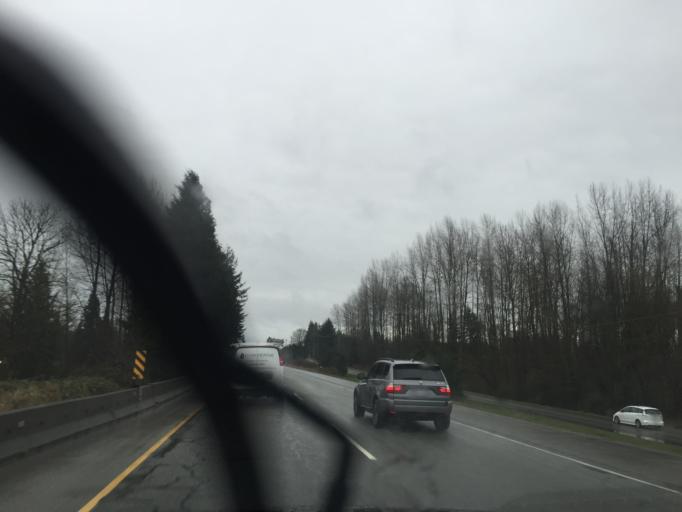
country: CA
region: British Columbia
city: Aldergrove
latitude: 49.0948
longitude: -122.4761
